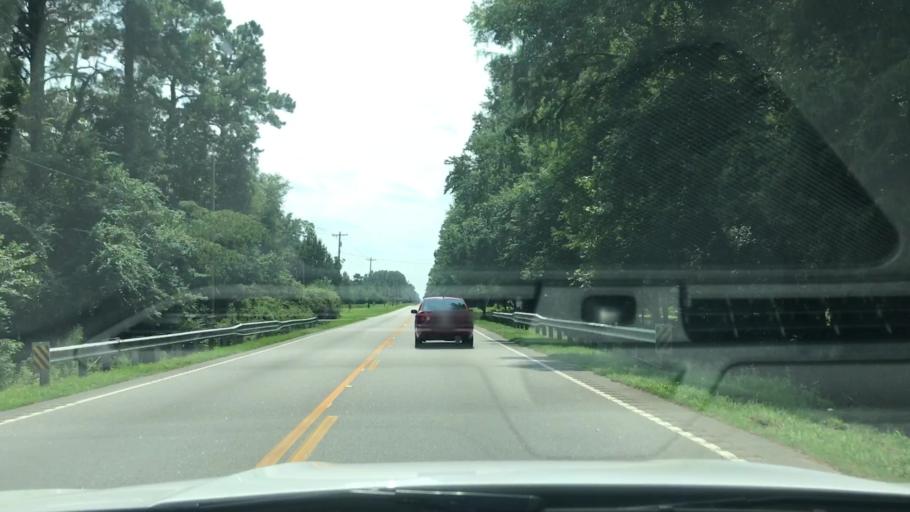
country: US
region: South Carolina
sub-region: Horry County
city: Conway
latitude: 33.7689
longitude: -79.0724
